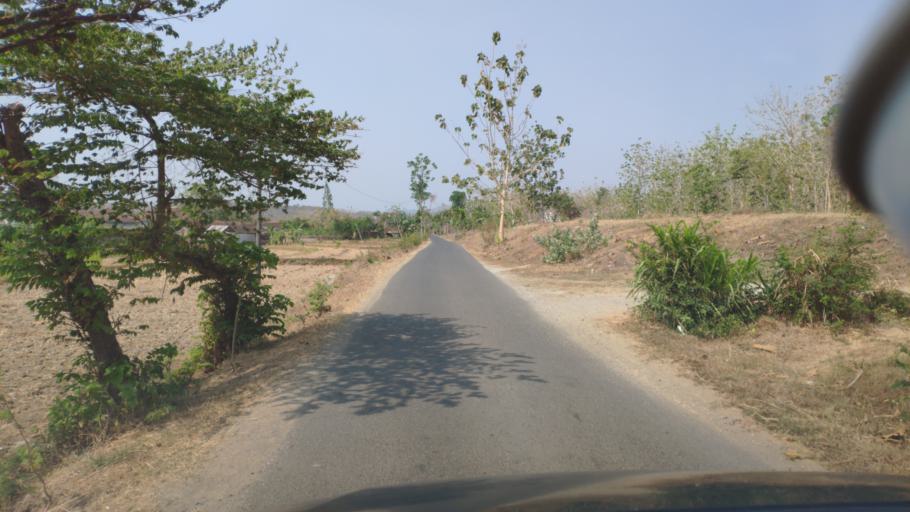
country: ID
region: Central Java
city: Ngadipurwo
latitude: -6.9166
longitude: 111.4538
